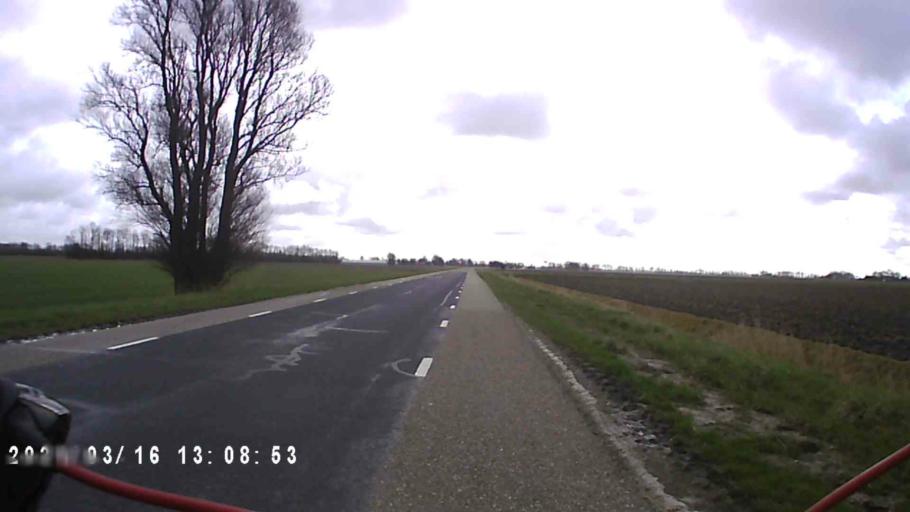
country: NL
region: Friesland
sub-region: Menameradiel
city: Berltsum
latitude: 53.2470
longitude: 5.6237
